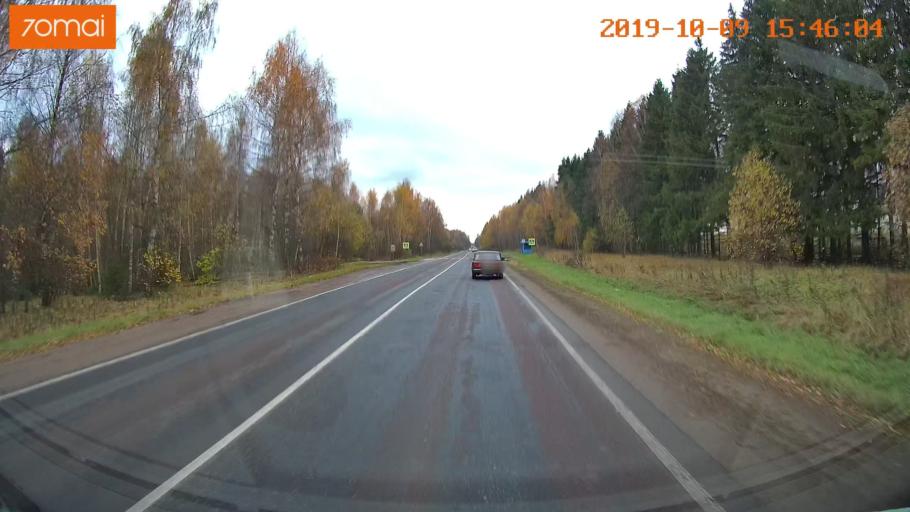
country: RU
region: Kostroma
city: Oktyabr'skiy
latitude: 57.8279
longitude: 41.0506
